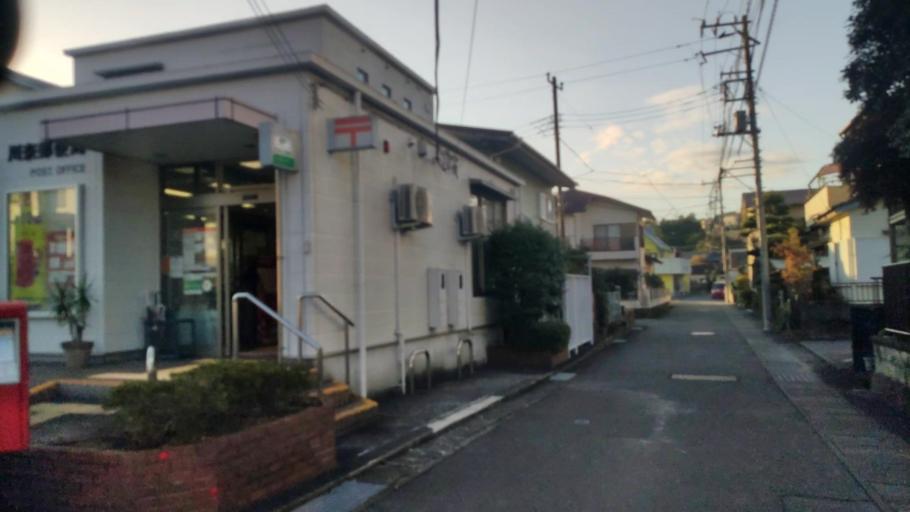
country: JP
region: Shizuoka
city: Ito
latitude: 34.9497
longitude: 139.1233
